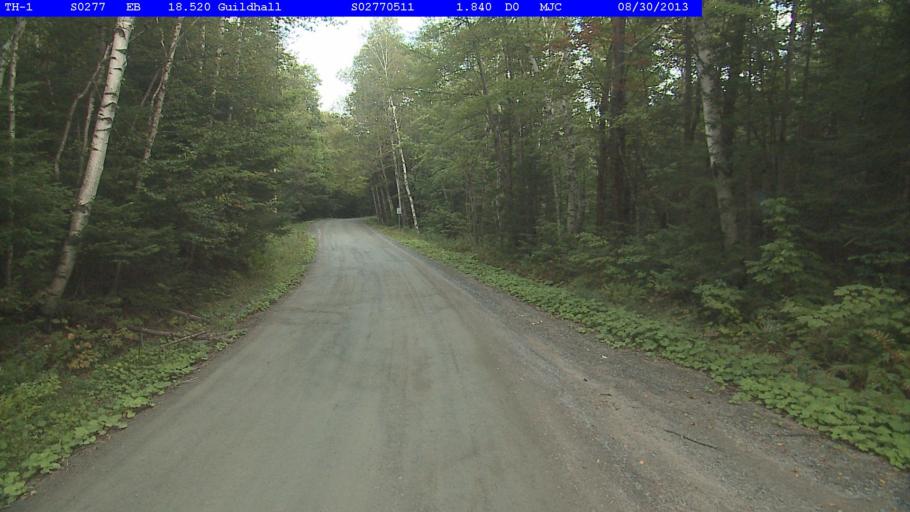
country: US
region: Vermont
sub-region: Essex County
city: Guildhall
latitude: 44.5629
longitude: -71.6379
